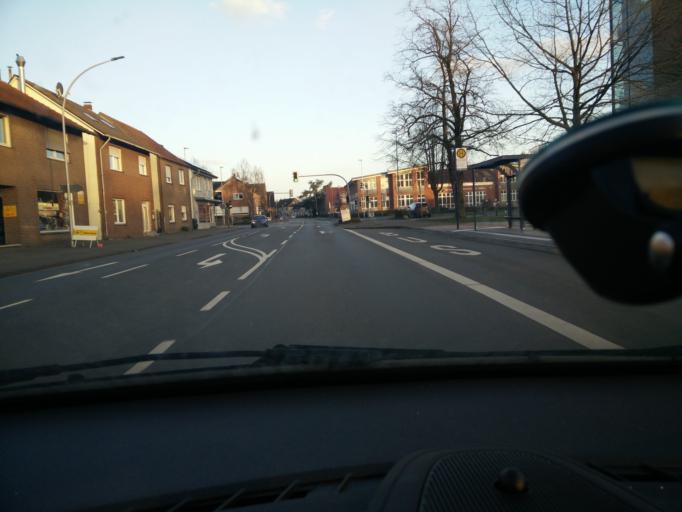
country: DE
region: North Rhine-Westphalia
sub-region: Regierungsbezirk Munster
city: Borken
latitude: 51.8408
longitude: 6.8687
